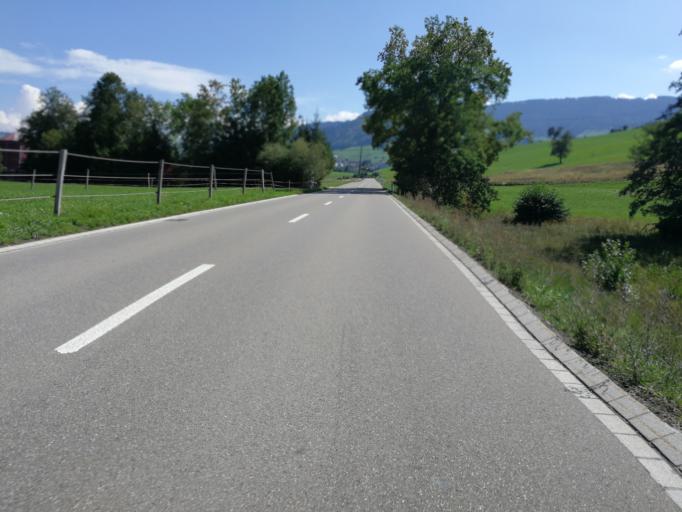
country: CH
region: Zurich
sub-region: Bezirk Horgen
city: Waedenswil / Eichweid
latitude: 47.2010
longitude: 8.6712
